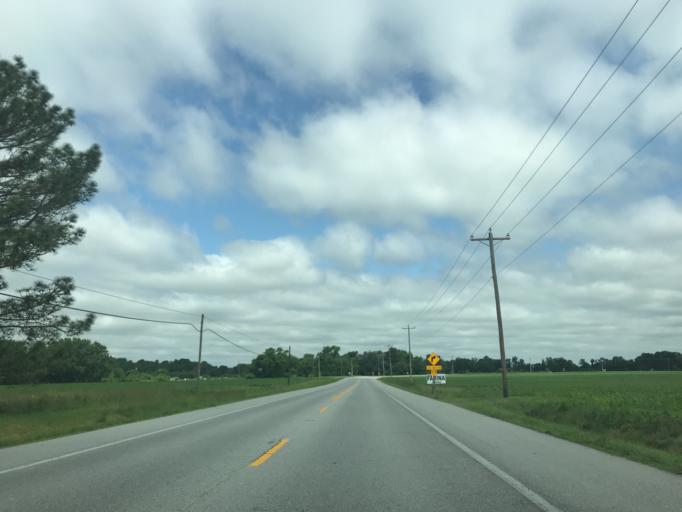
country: US
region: Maryland
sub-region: Caroline County
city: Ridgely
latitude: 38.9573
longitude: -75.8886
